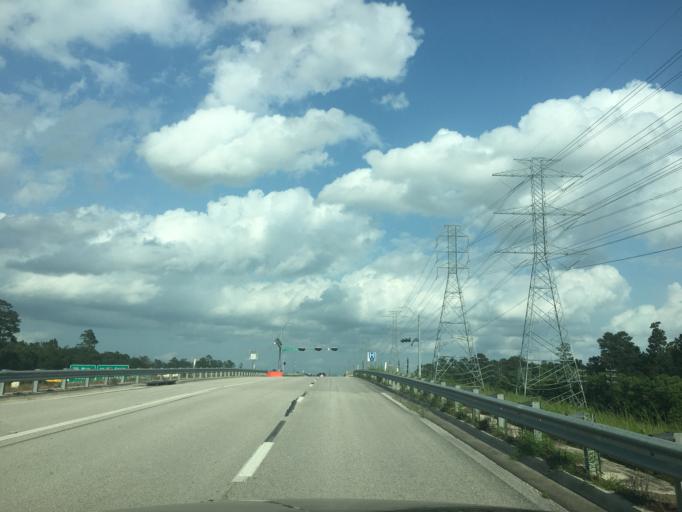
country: US
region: Texas
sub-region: Harris County
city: Spring
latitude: 30.0887
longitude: -95.4587
